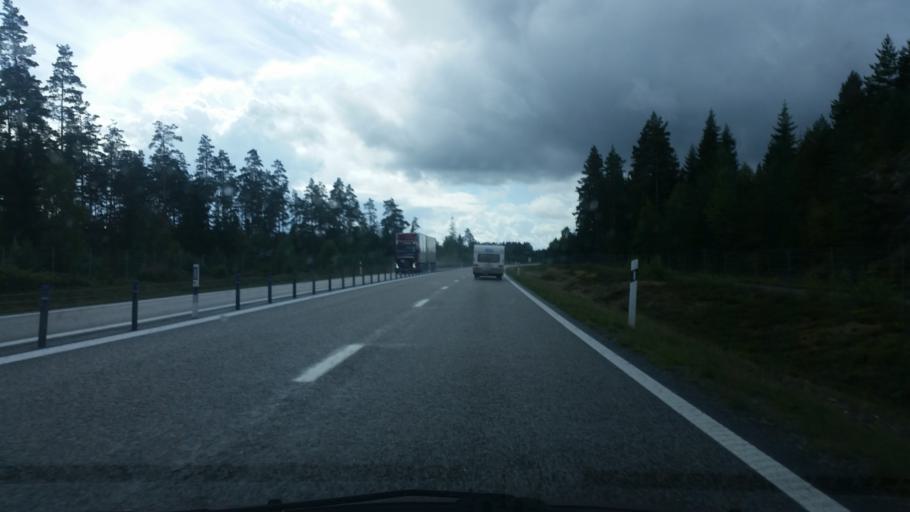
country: SE
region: Joenkoeping
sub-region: Gislaveds Kommun
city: Gislaved
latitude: 57.3487
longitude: 13.5560
